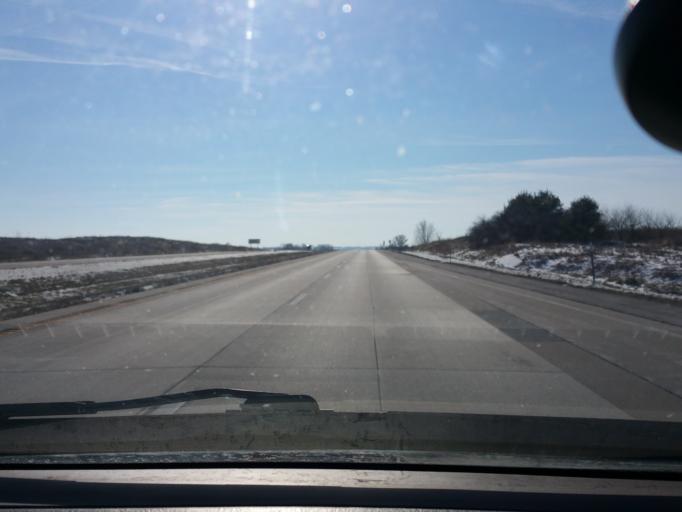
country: US
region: Missouri
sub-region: Daviess County
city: Gallatin
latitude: 40.0725
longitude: -94.0937
